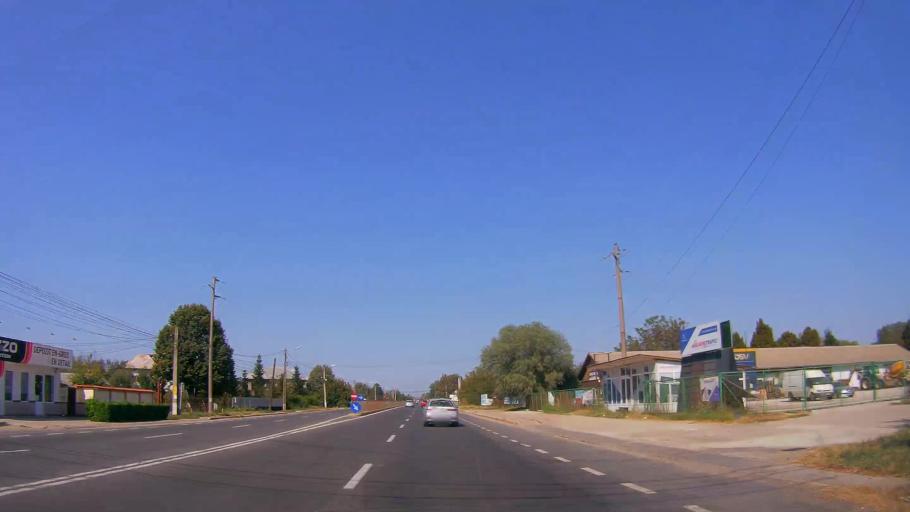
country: RO
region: Giurgiu
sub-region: Comuna Fratesti
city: Remus
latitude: 43.9317
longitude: 25.9761
